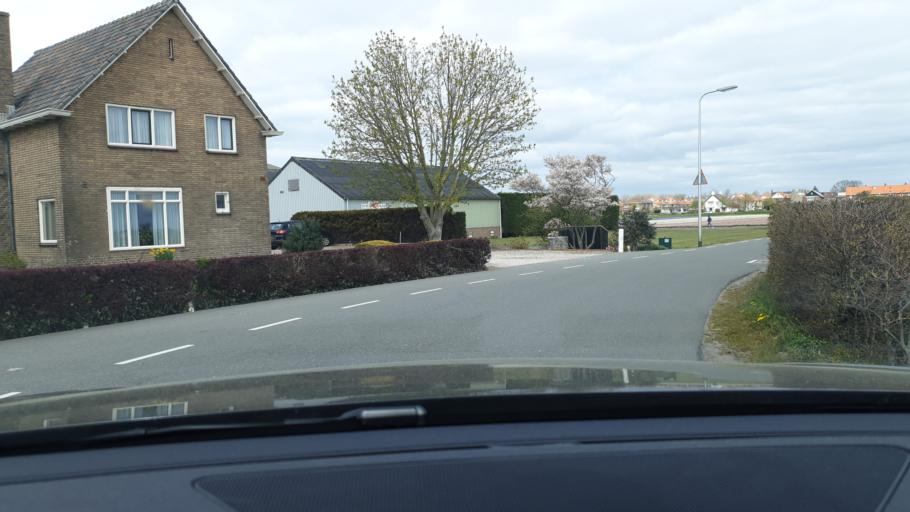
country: NL
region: South Holland
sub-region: Gemeente Lisse
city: Lisse
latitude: 52.2981
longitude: 4.5415
